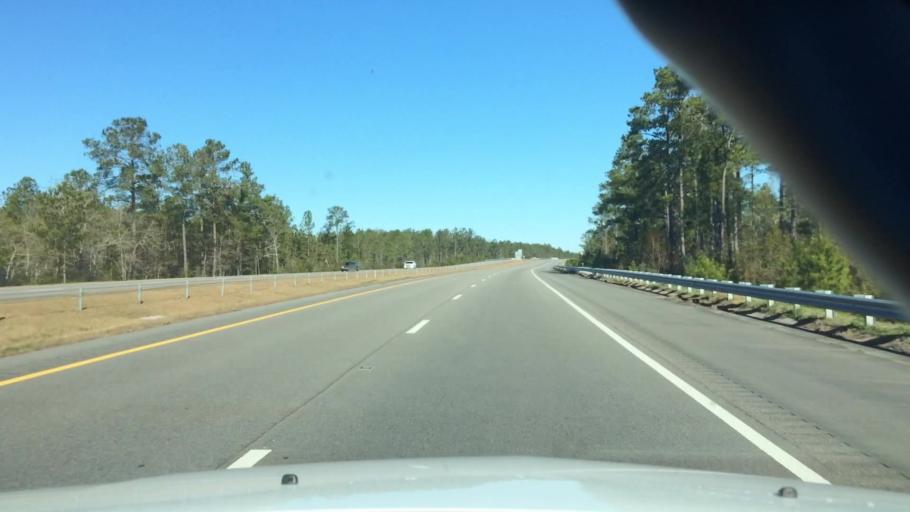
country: US
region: North Carolina
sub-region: Brunswick County
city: Leland
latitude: 34.2140
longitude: -78.0766
